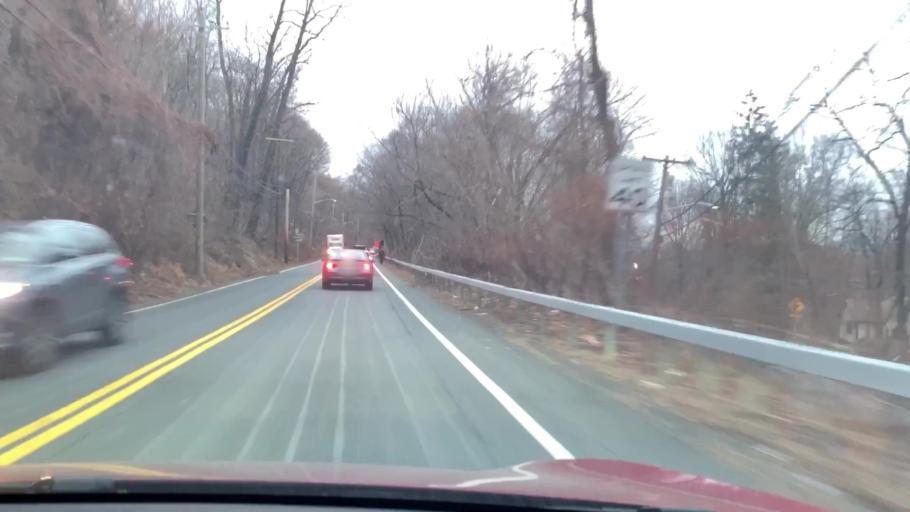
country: US
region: New York
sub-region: Rockland County
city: South Nyack
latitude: 41.0732
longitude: -73.9228
